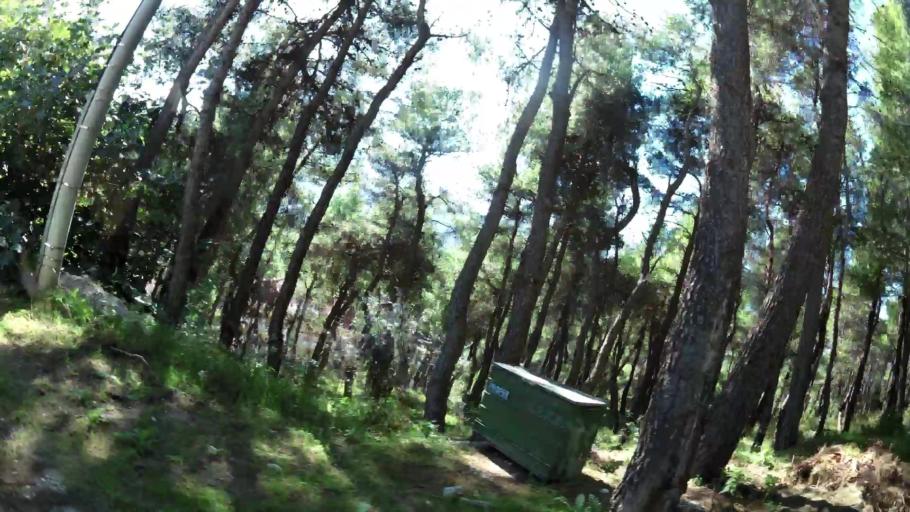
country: GR
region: Attica
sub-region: Nomarchia Anatolikis Attikis
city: Dionysos
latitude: 38.1042
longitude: 23.8813
